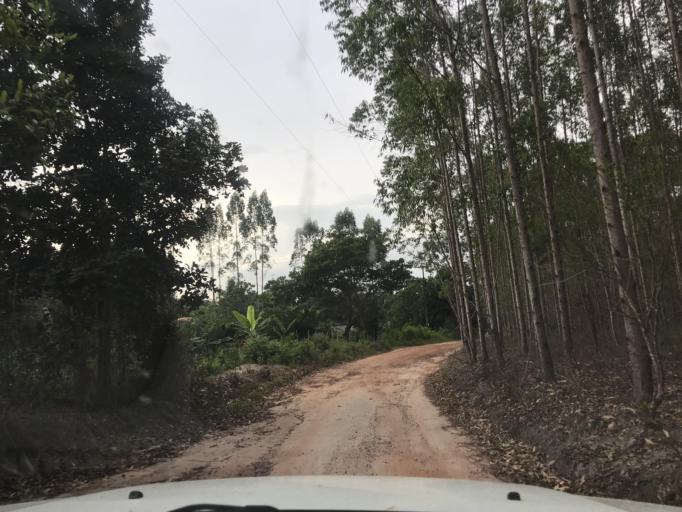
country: BR
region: Bahia
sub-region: Entre Rios
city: Entre Rios
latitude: -12.0985
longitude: -38.1899
